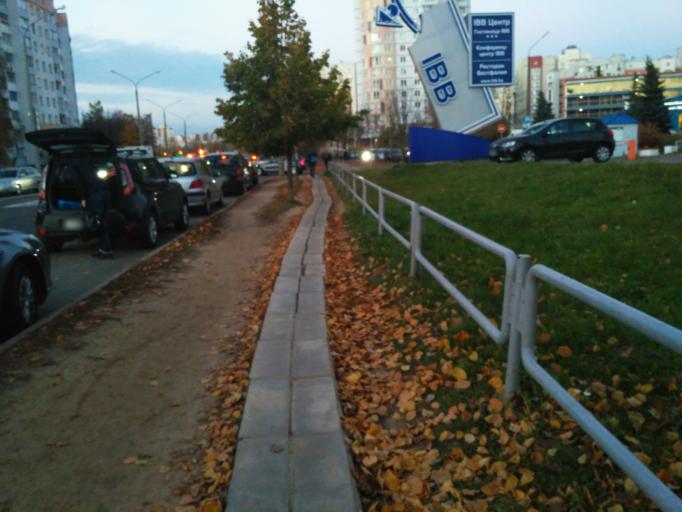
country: BY
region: Minsk
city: Novoye Medvezhino
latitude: 53.8683
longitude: 27.4855
